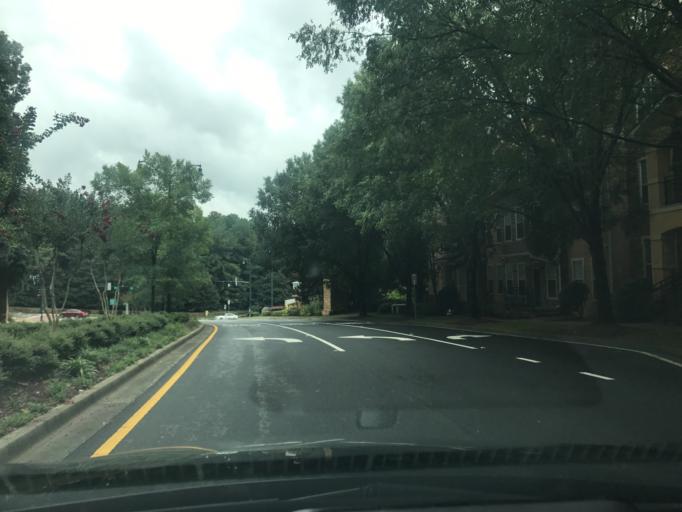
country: US
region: Georgia
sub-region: DeKalb County
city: Dunwoody
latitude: 33.9138
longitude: -84.3395
